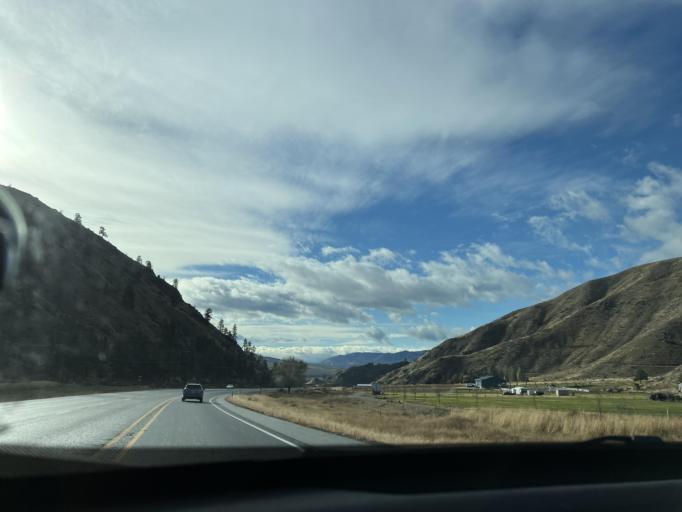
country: US
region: Washington
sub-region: Chelan County
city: Manson
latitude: 47.7905
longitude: -120.1344
